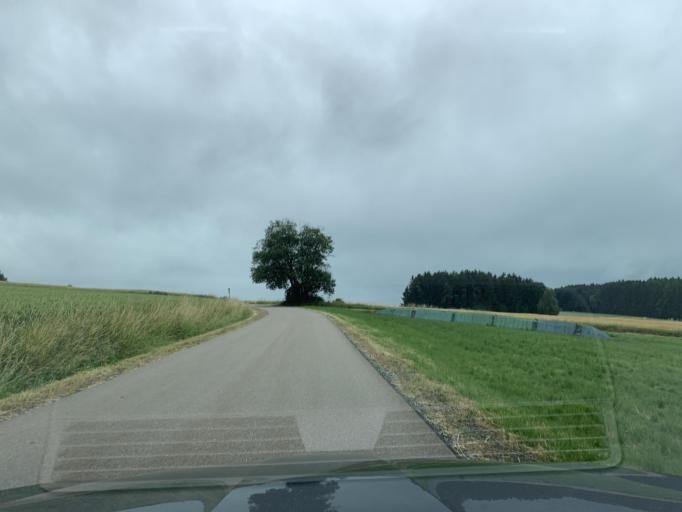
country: DE
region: Bavaria
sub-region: Upper Palatinate
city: Winklarn
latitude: 49.4178
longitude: 12.4490
